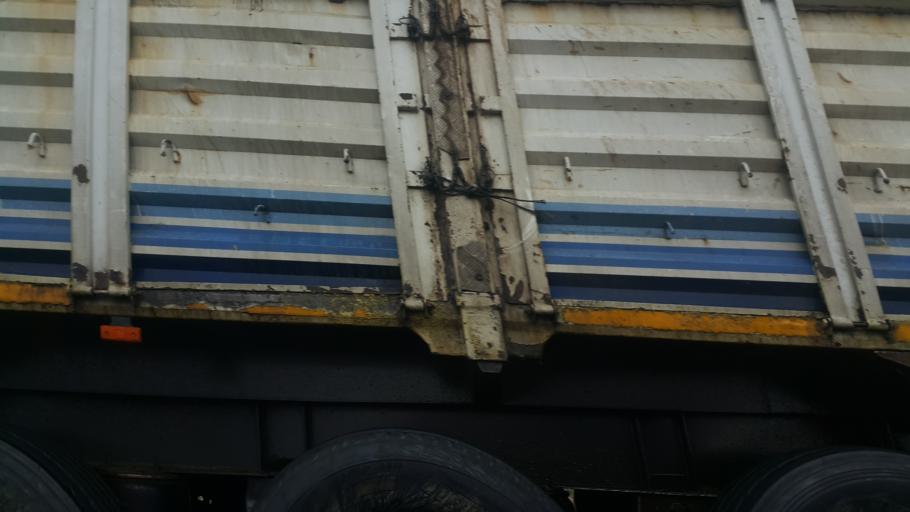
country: TR
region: Aksaray
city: Taspinar
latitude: 38.1206
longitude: 34.0340
